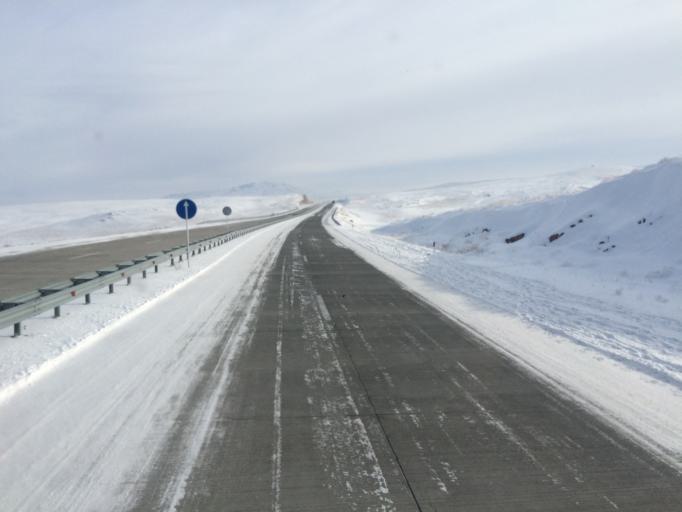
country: KZ
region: Zhambyl
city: Georgiyevka
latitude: 43.4220
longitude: 74.9677
